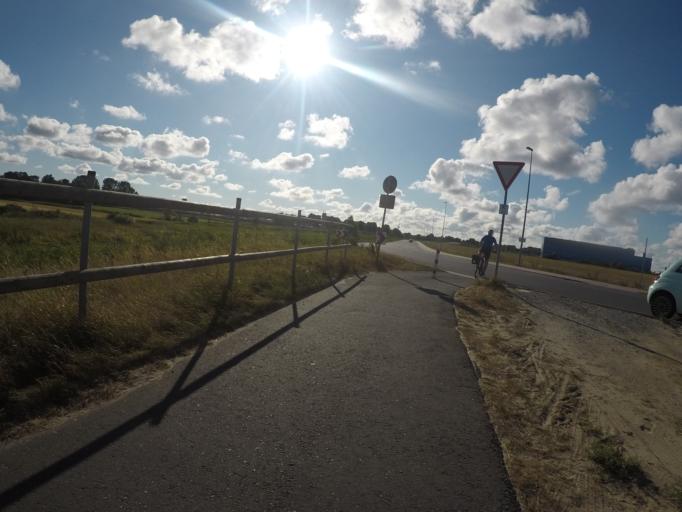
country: DE
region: Lower Saxony
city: Cuxhaven
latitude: 53.8406
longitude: 8.7481
